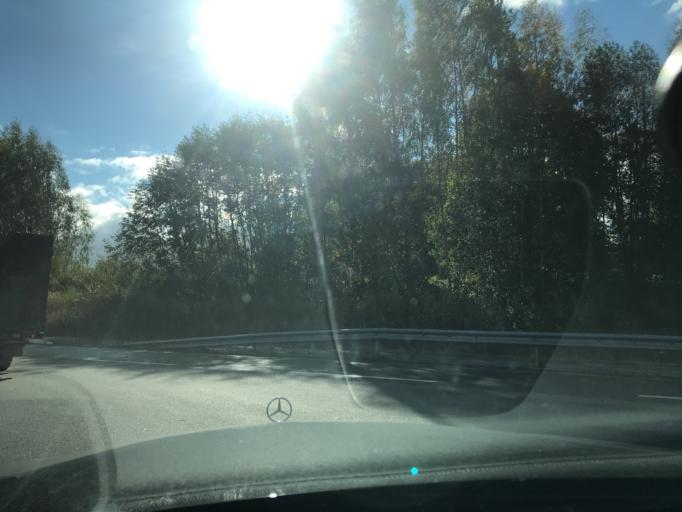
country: EE
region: Vorumaa
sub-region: Voru linn
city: Voru
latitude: 57.8097
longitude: 27.0643
